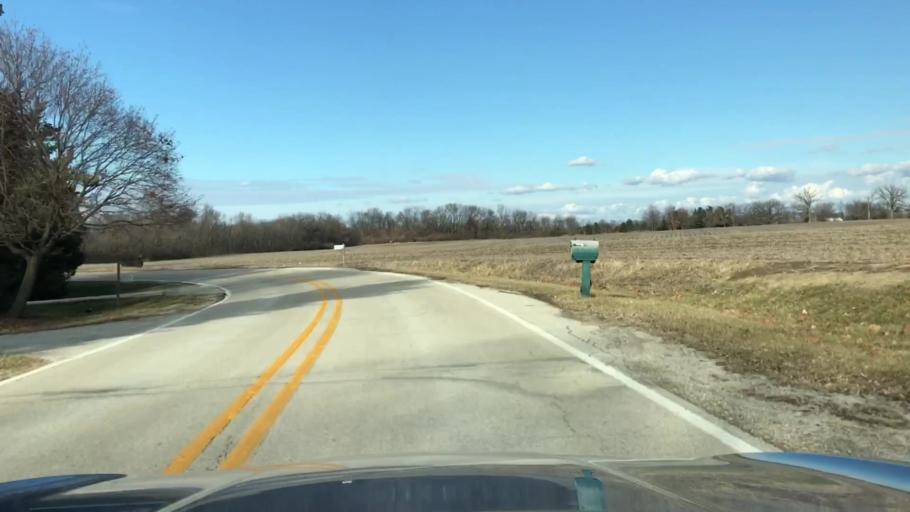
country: US
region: Illinois
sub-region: McLean County
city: Hudson
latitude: 40.6520
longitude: -88.9208
